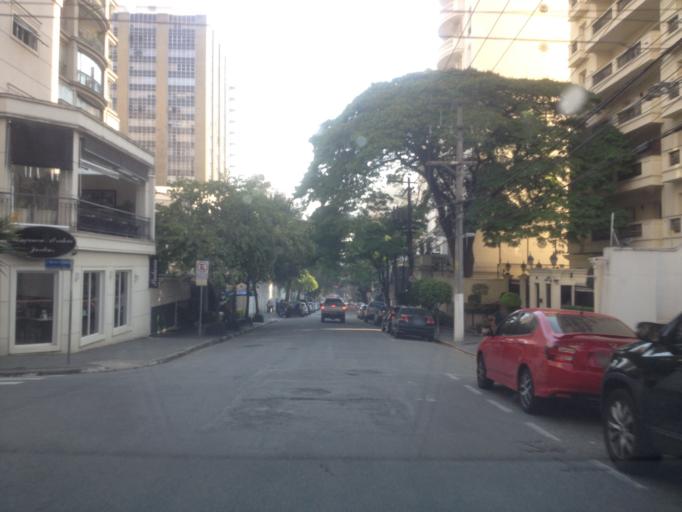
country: BR
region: Sao Paulo
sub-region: Sao Paulo
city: Sao Paulo
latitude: -23.5630
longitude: -46.6634
